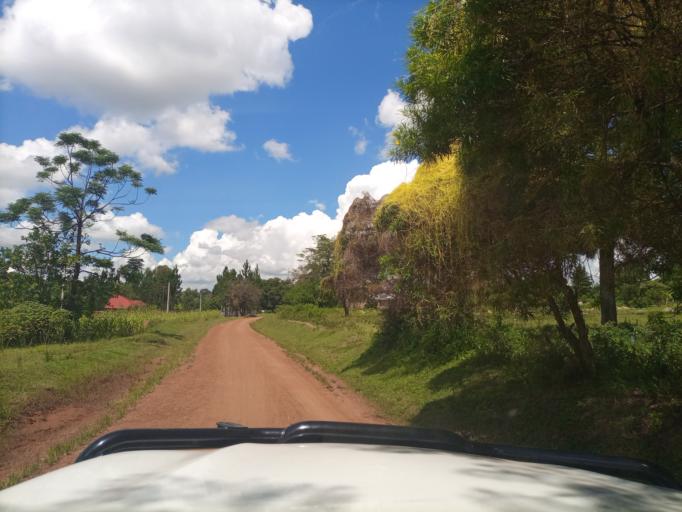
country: UG
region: Eastern Region
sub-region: Tororo District
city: Tororo
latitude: 0.6991
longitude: 34.0127
